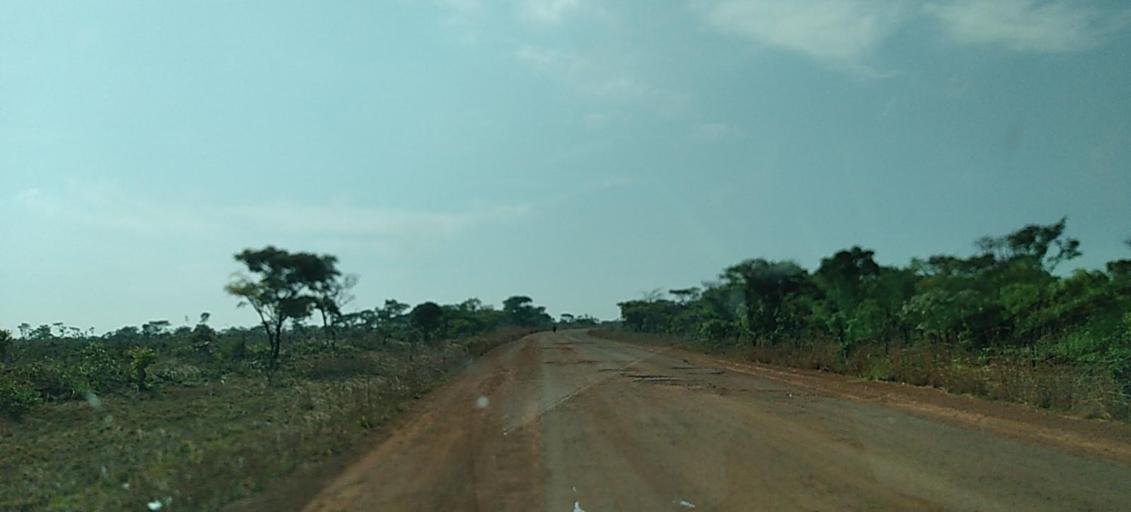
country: ZM
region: North-Western
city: Mwinilunga
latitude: -11.7761
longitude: 25.0187
